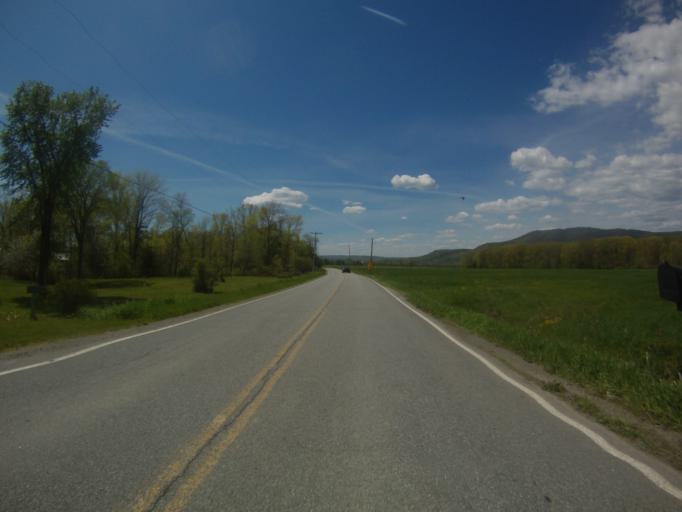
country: US
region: New York
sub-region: Essex County
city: Port Henry
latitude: 43.9962
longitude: -73.4195
